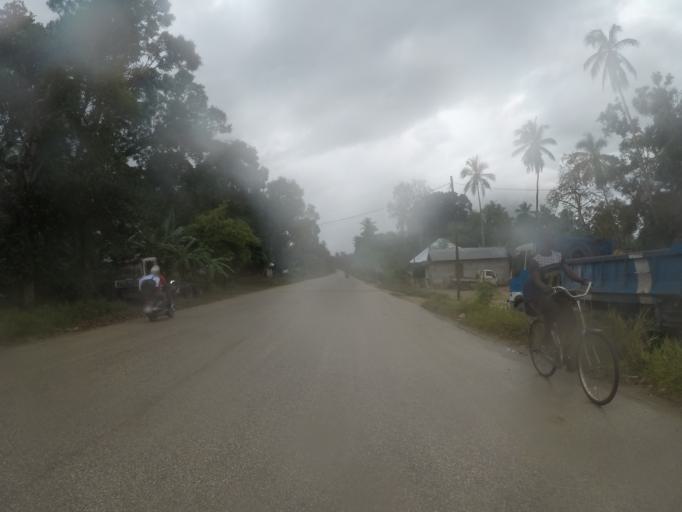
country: TZ
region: Zanzibar Central/South
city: Koani
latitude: -6.0408
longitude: 39.2225
